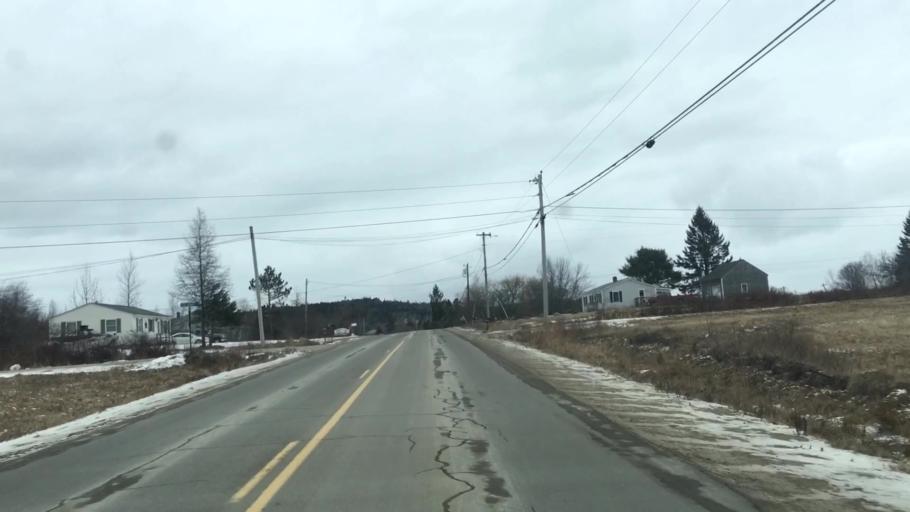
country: US
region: Maine
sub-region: Washington County
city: Machiasport
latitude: 44.7112
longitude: -67.4029
